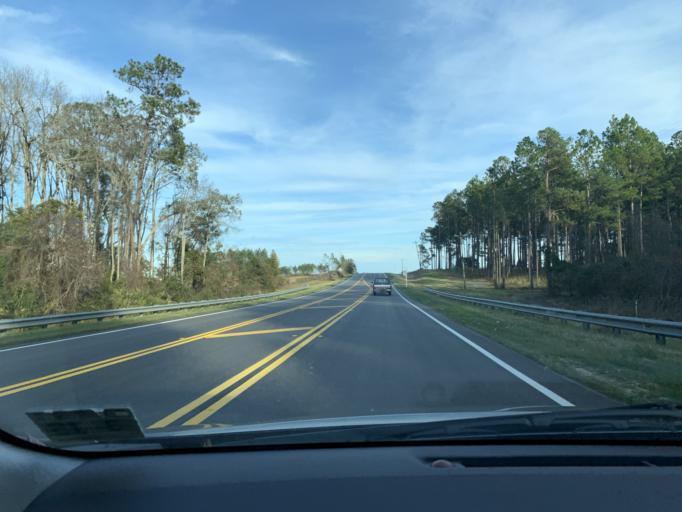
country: US
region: Georgia
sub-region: Irwin County
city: Ocilla
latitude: 31.5939
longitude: -83.1903
